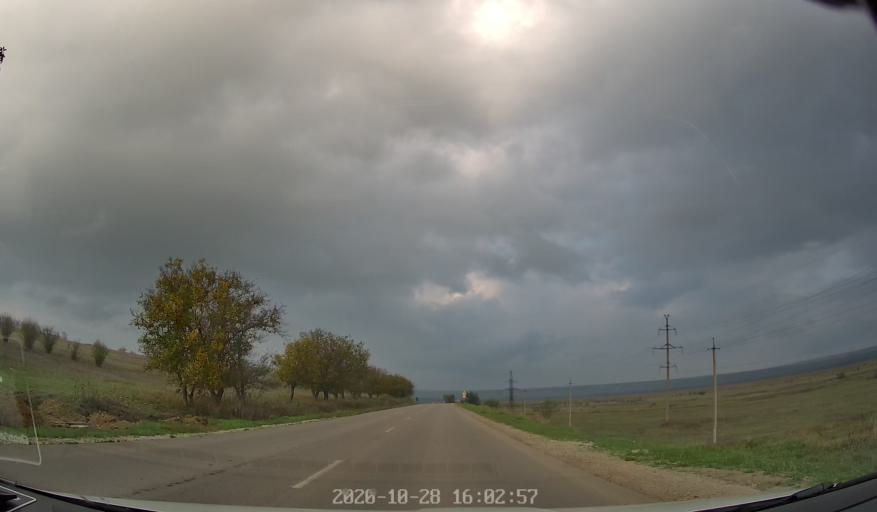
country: UA
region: Odessa
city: Zaliznychne
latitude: 45.7956
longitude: 28.5709
